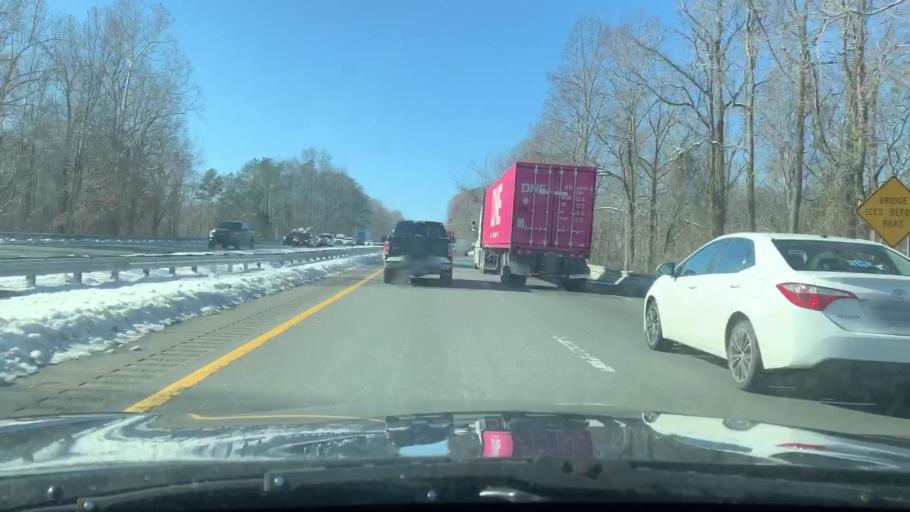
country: US
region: North Carolina
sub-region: Orange County
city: Hillsborough
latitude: 36.0585
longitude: -79.0882
